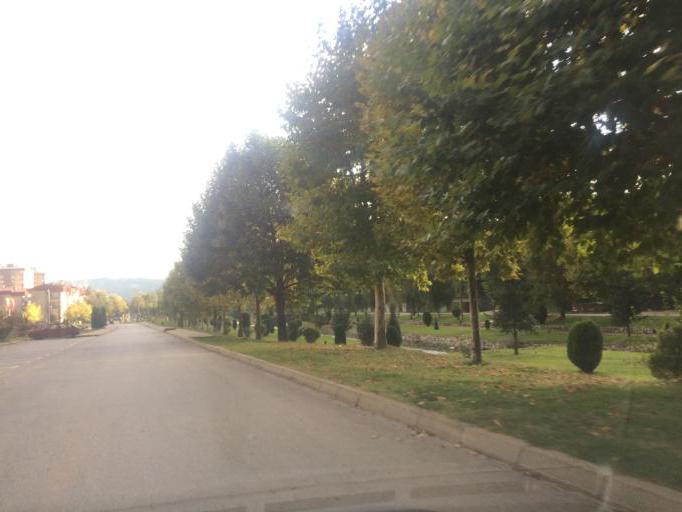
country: MK
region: Makedonska Kamenica
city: Makedonska Kamenica
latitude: 42.0229
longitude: 22.5876
